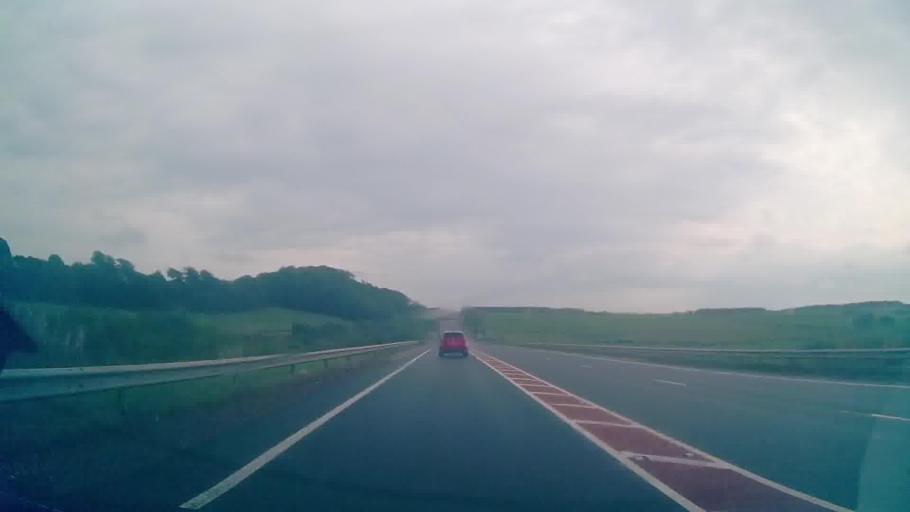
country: GB
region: Scotland
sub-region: Dumfries and Galloway
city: Lockerbie
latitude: 55.0276
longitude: -3.3878
